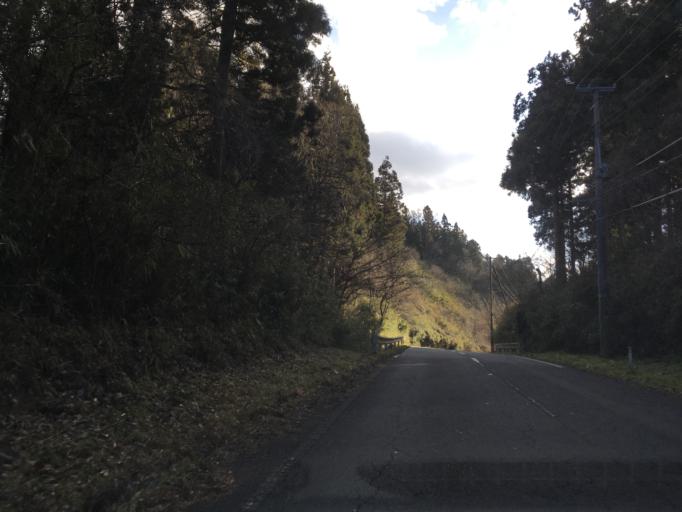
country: JP
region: Iwate
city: Ichinoseki
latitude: 38.8124
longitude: 140.9971
